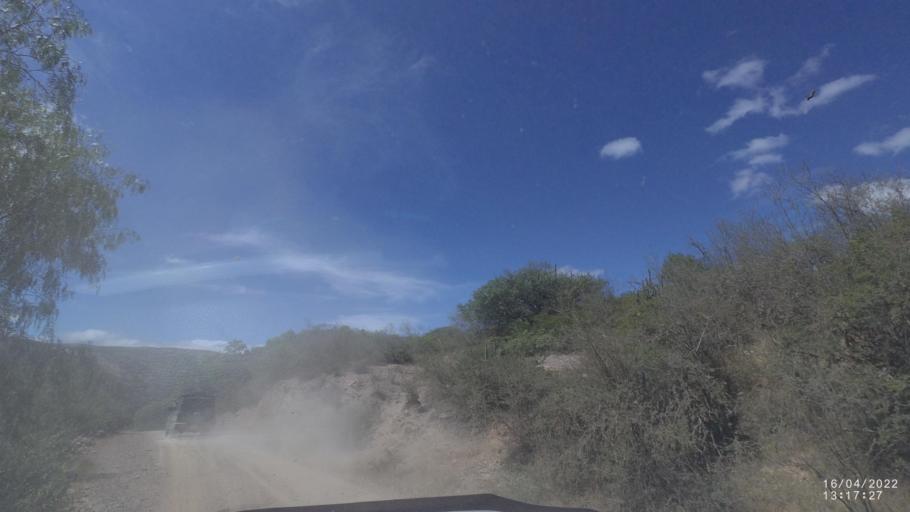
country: BO
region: Cochabamba
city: Mizque
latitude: -17.9888
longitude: -65.6218
